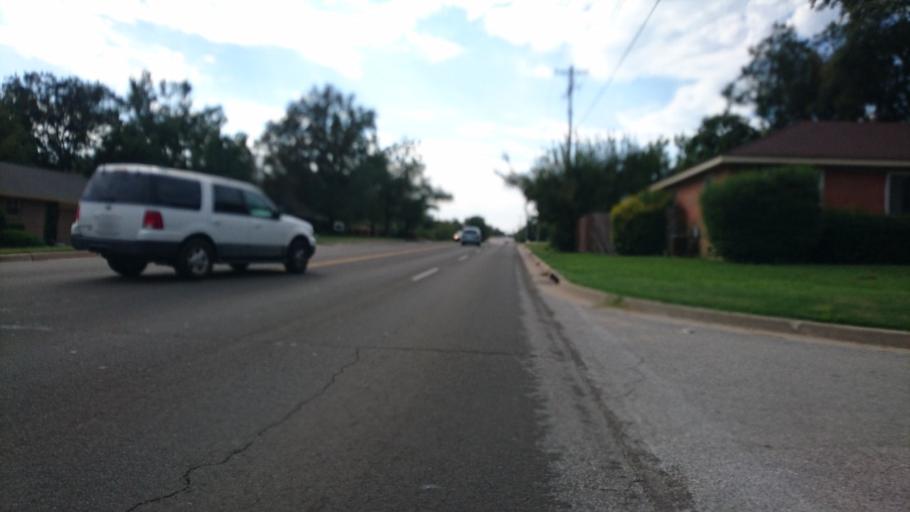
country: US
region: Oklahoma
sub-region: Oklahoma County
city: Nichols Hills
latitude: 35.5077
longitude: -97.5709
